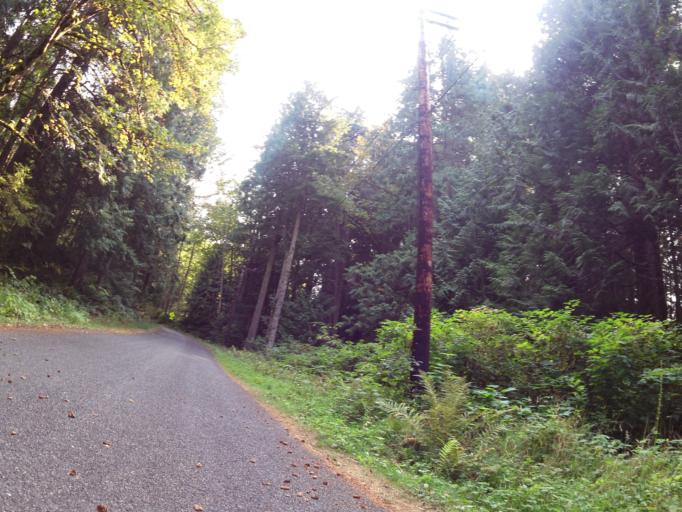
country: US
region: Washington
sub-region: Whatcom County
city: Bellingham
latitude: 48.6999
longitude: -122.4902
